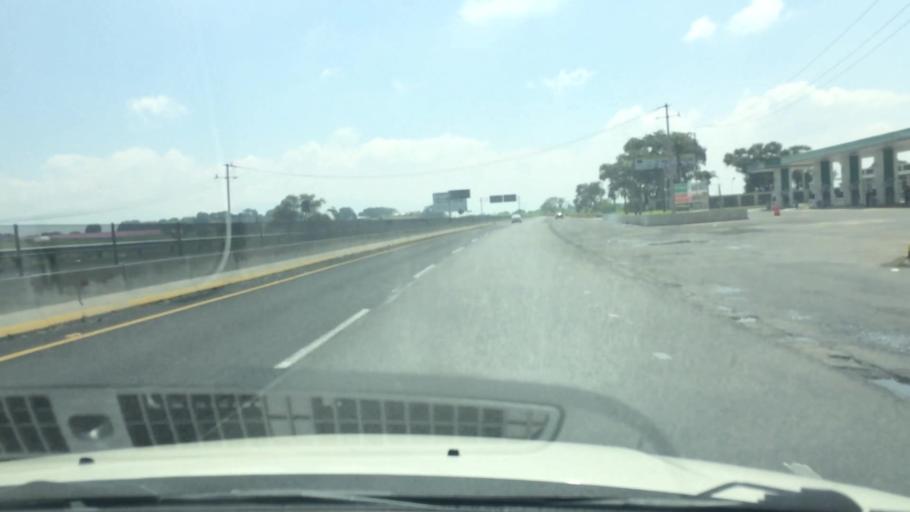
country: MX
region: Mexico
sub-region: Temoaya
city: Llano de la Y
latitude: 19.4102
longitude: -99.6145
